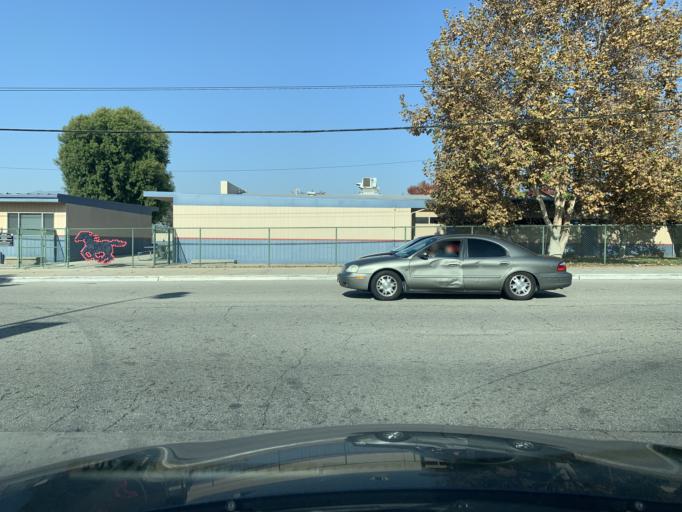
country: US
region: California
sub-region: Los Angeles County
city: Covina
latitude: 34.0752
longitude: -117.8824
